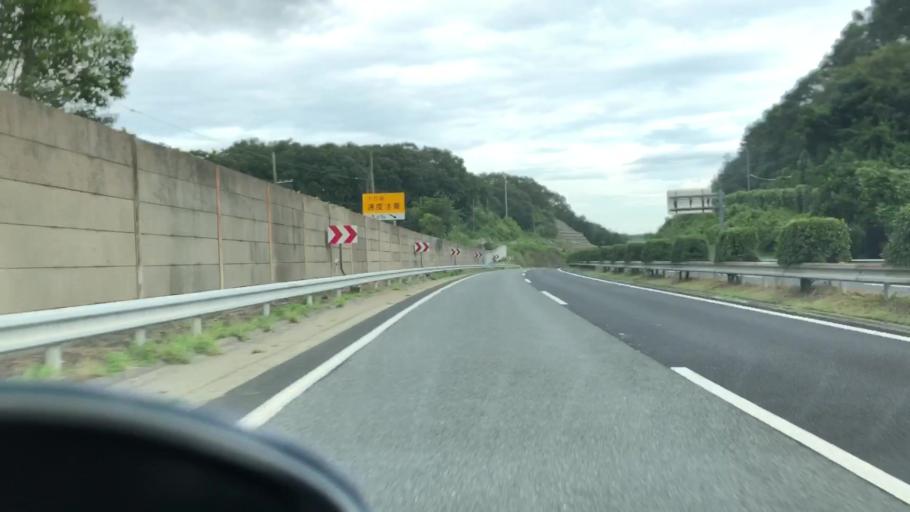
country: JP
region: Hyogo
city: Yashiro
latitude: 34.8923
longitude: 135.0894
